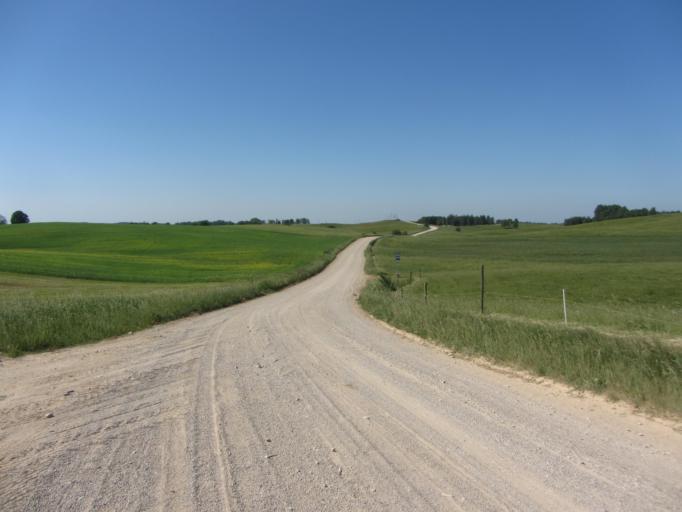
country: LT
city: Ziezmariai
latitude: 54.7242
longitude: 24.3934
